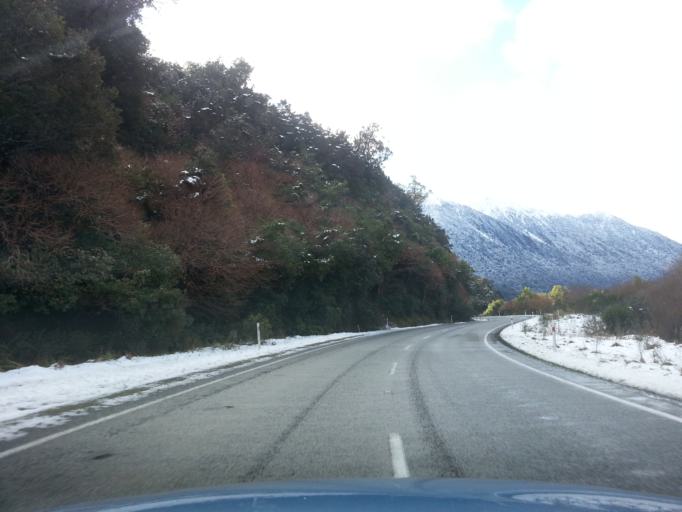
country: NZ
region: West Coast
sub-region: Grey District
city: Greymouth
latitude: -42.8208
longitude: 171.5630
